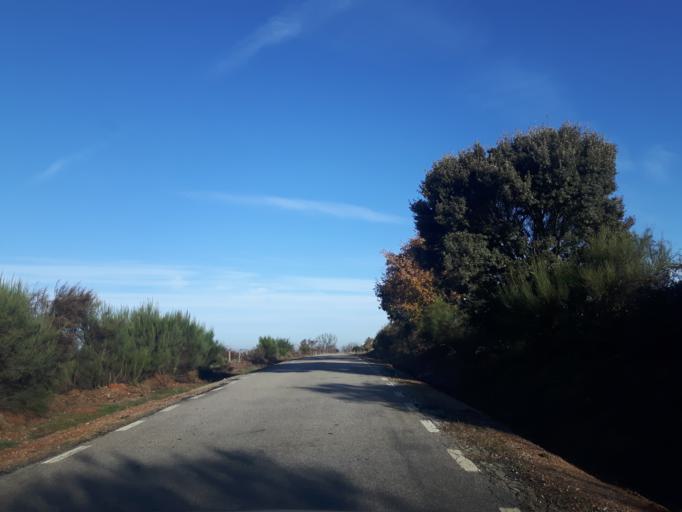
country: ES
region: Castille and Leon
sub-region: Provincia de Salamanca
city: Olmedo de Camaces
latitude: 40.9087
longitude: -6.6184
